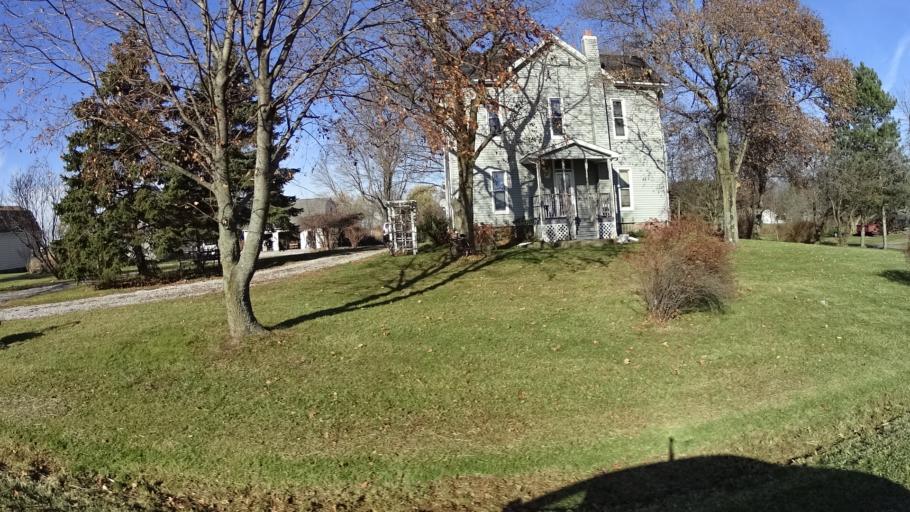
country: US
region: Ohio
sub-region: Lorain County
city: Wellington
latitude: 41.1149
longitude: -82.2393
